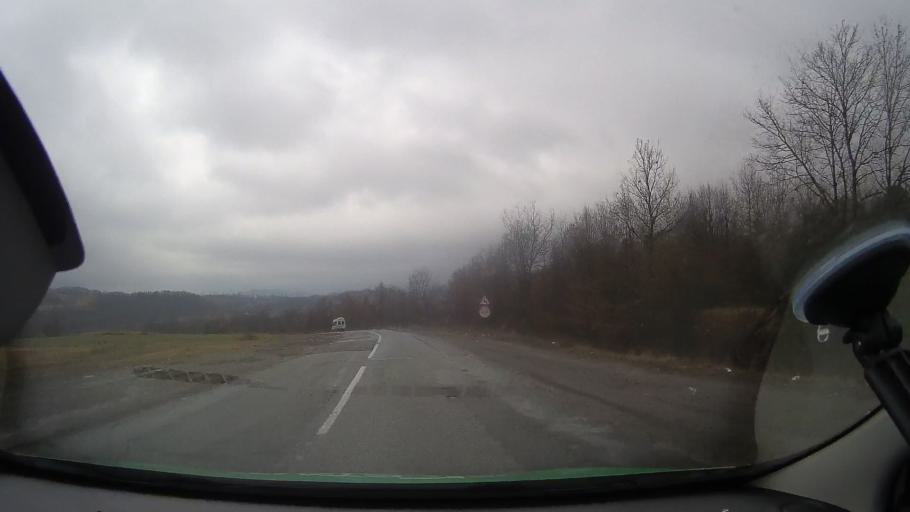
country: RO
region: Arad
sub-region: Comuna Varfurile
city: Varfurile
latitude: 46.2933
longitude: 22.5415
